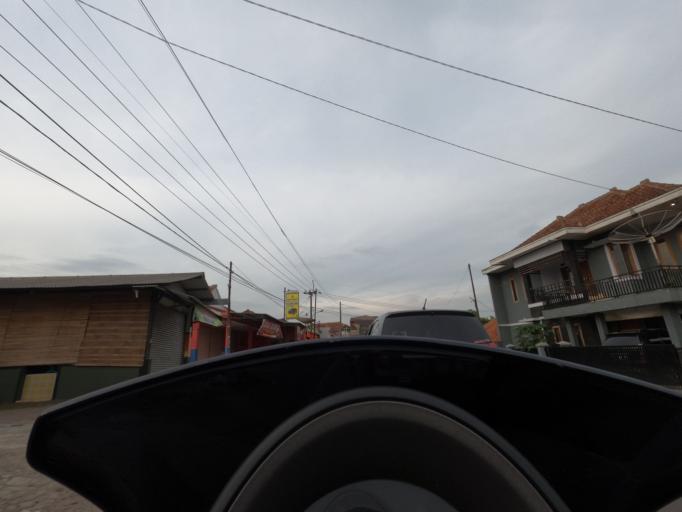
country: ID
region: West Java
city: Lembang
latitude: -6.6573
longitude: 107.7135
